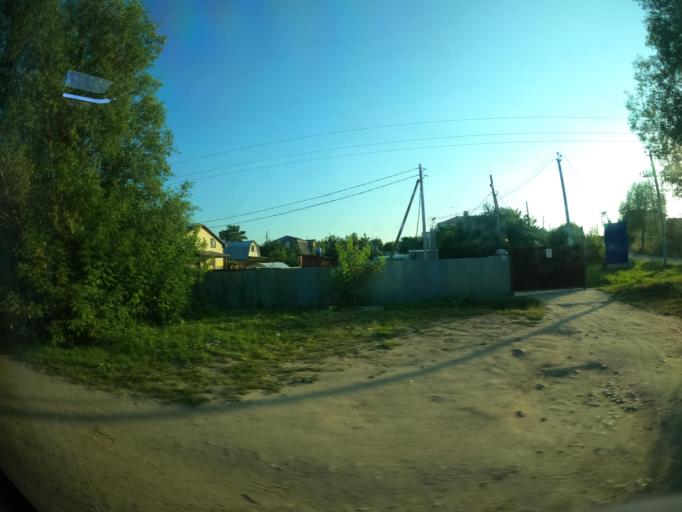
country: RU
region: Moskovskaya
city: Serpukhov
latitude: 54.9416
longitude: 37.3526
